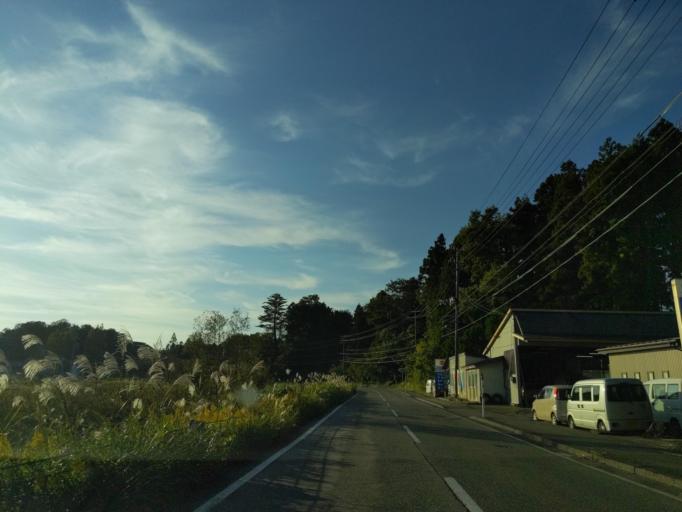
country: JP
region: Niigata
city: Nagaoka
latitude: 37.5790
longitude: 138.7642
